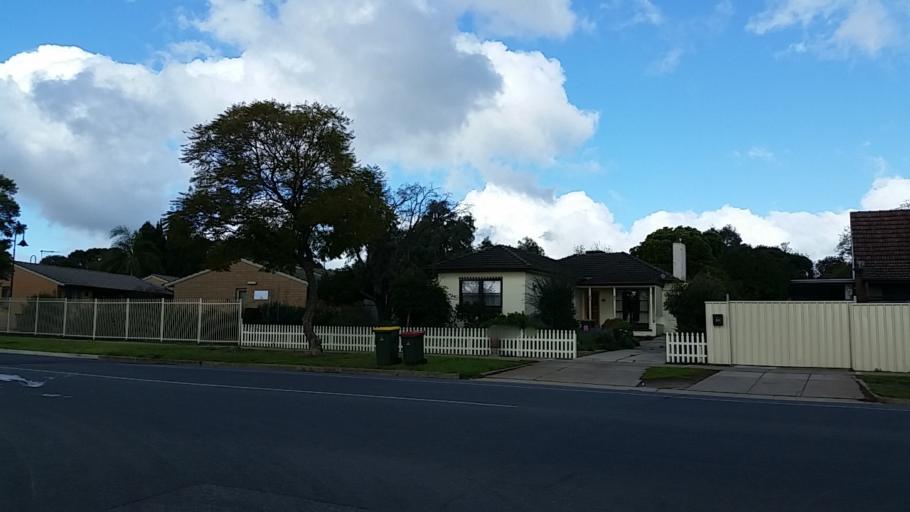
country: AU
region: South Australia
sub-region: Salisbury
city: Elizabeth
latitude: -34.7243
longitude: 138.6813
